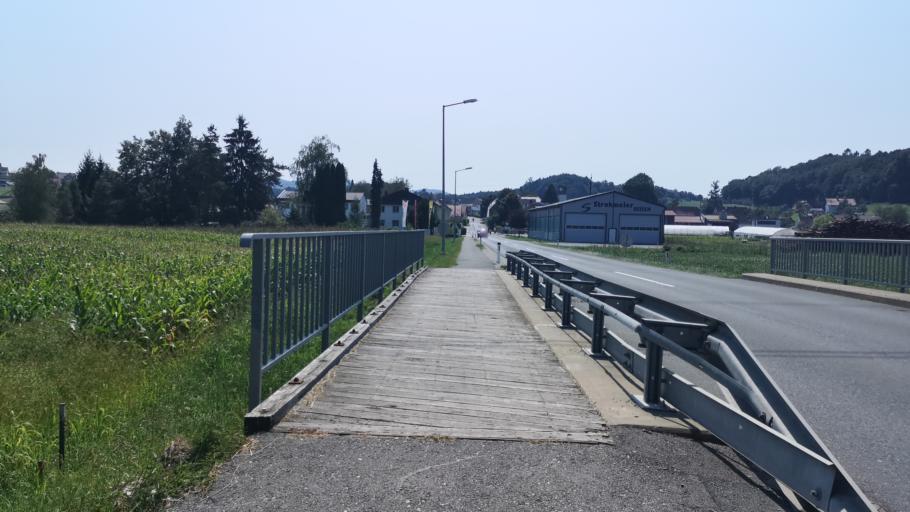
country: AT
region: Styria
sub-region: Politischer Bezirk Deutschlandsberg
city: Wettmannstatten
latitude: 46.8342
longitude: 15.3825
